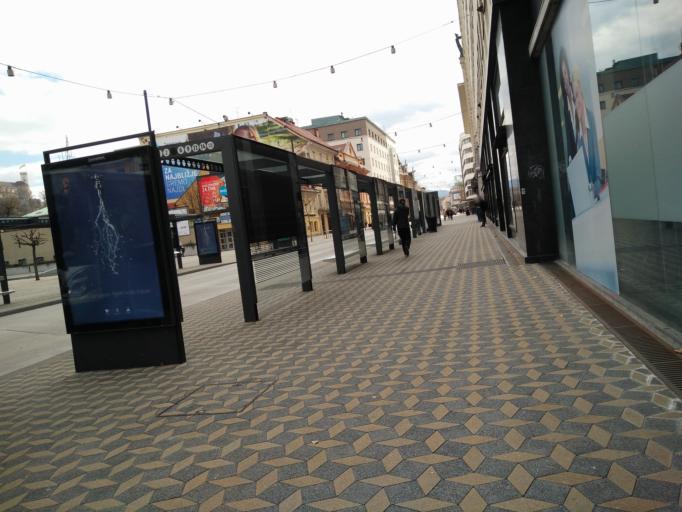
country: SI
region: Ljubljana
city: Ljubljana
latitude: 46.0539
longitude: 14.5041
